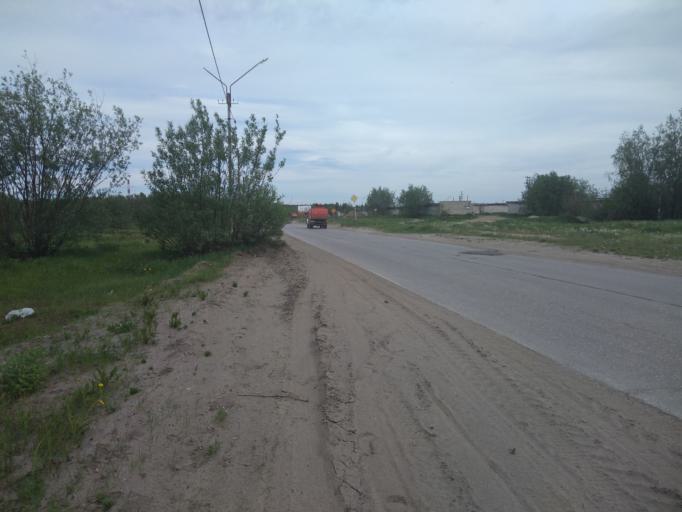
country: RU
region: Komi Republic
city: Pechora
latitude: 65.1432
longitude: 57.2462
